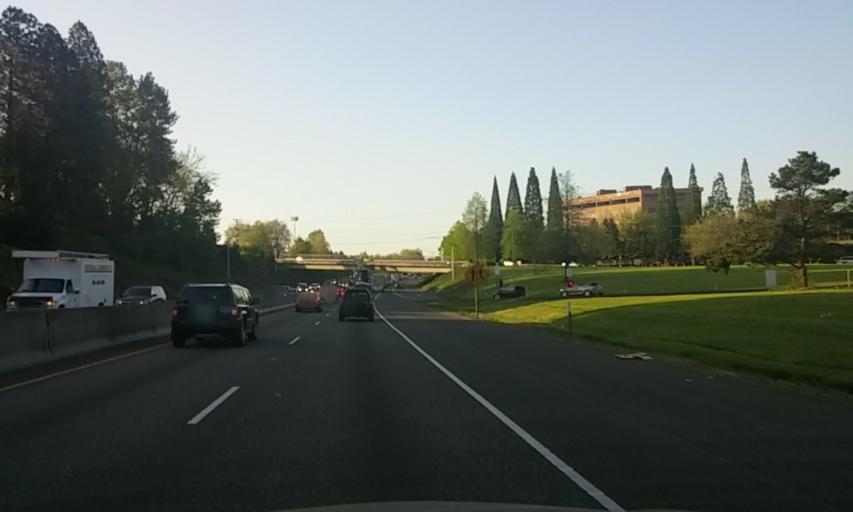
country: US
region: Oregon
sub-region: Washington County
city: Garden Home-Whitford
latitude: 45.4598
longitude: -122.7852
